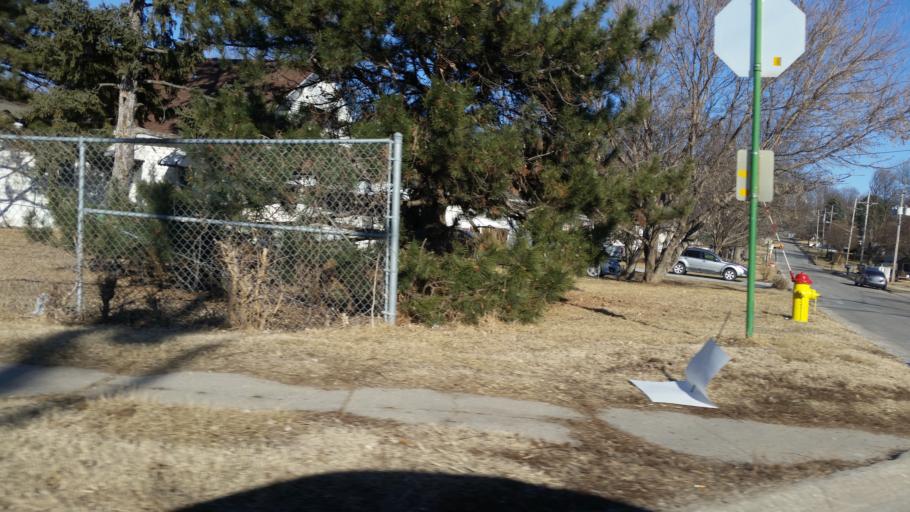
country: US
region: Nebraska
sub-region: Sarpy County
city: Bellevue
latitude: 41.1635
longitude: -95.9226
